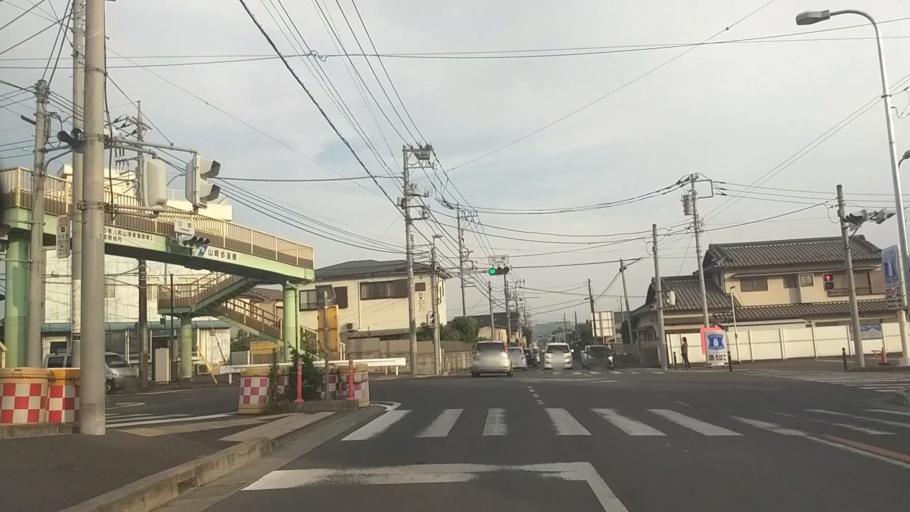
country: JP
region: Kanagawa
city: Odawara
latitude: 35.3070
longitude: 139.1233
